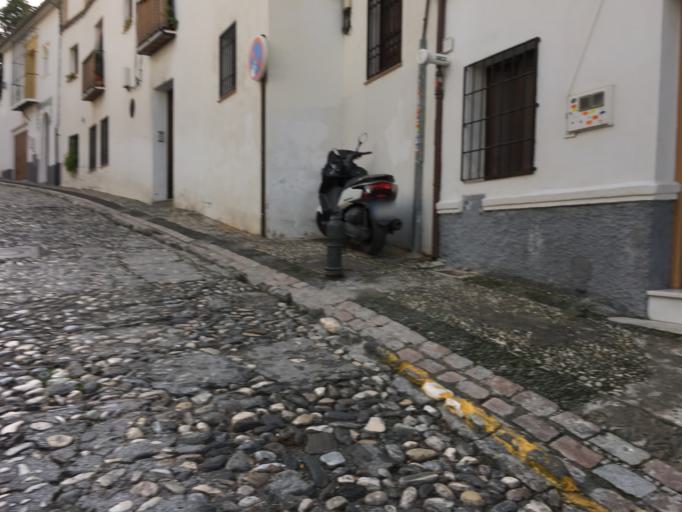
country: ES
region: Andalusia
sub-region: Provincia de Granada
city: Granada
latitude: 37.1823
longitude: -3.5965
